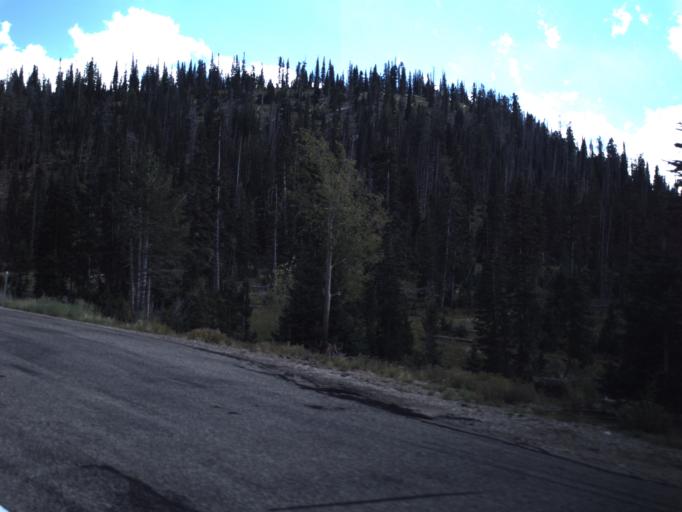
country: US
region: Utah
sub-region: Iron County
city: Cedar City
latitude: 37.5676
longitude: -112.8494
